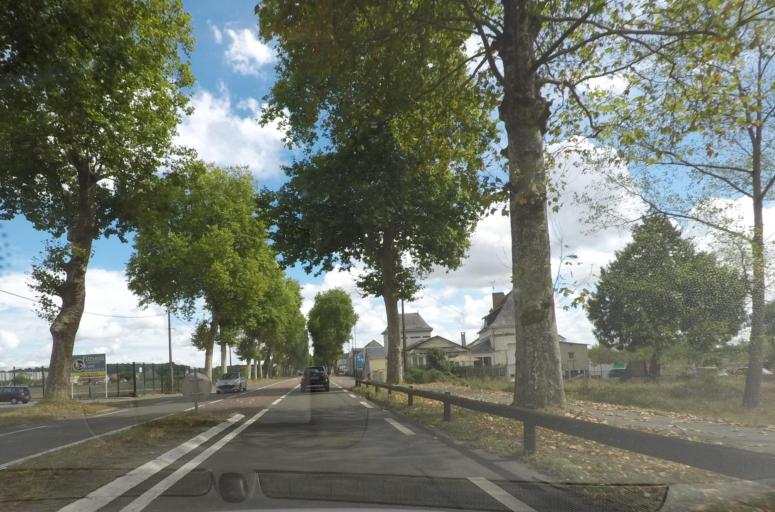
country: FR
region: Pays de la Loire
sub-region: Departement de la Sarthe
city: La Fleche
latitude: 47.6982
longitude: -0.0607
